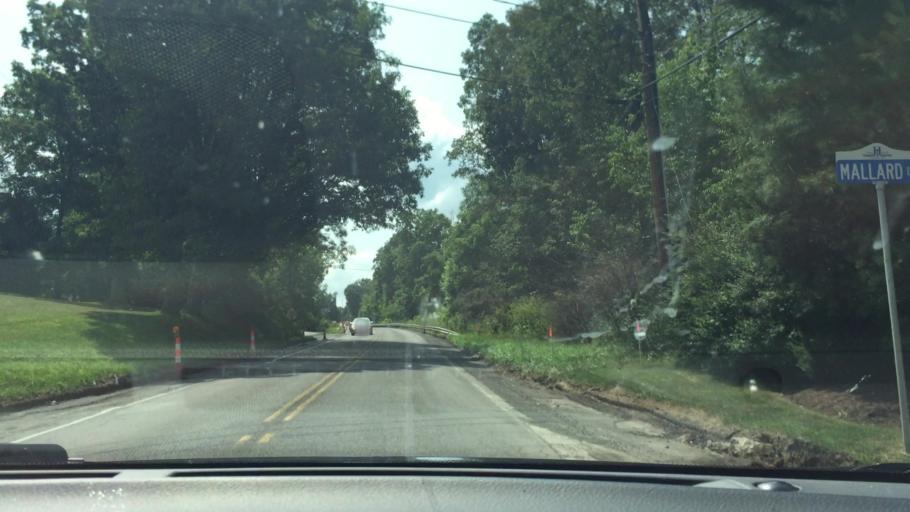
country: US
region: Pennsylvania
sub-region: Allegheny County
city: Gibsonia
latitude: 40.6138
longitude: -79.9514
